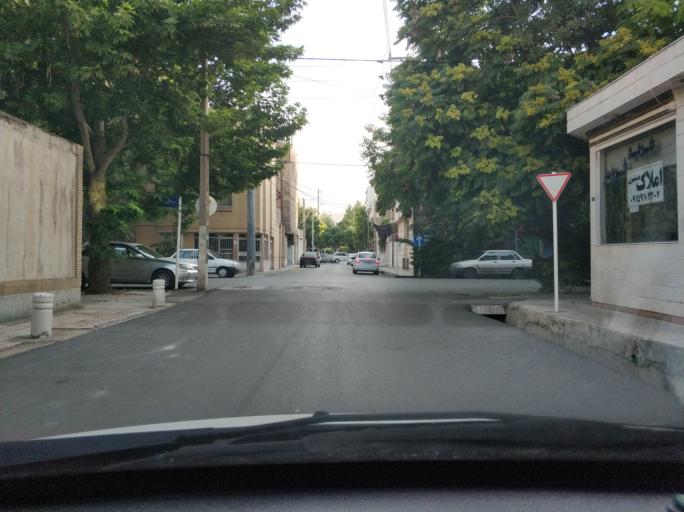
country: IR
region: Razavi Khorasan
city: Mashhad
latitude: 36.2719
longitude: 59.5963
